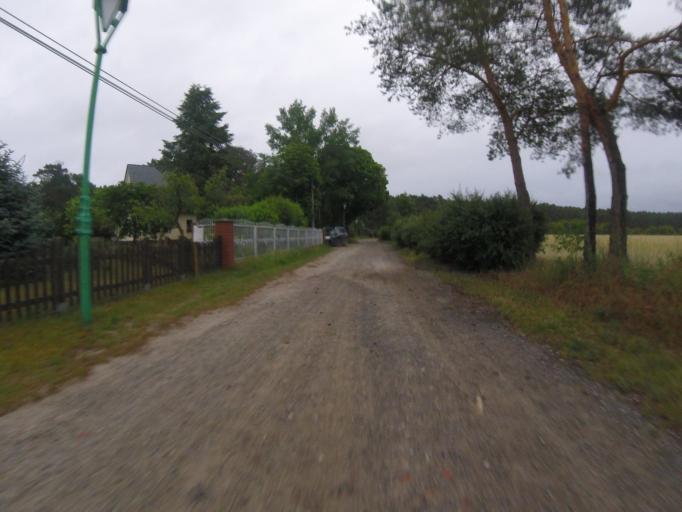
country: DE
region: Brandenburg
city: Bestensee
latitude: 52.2352
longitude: 13.7201
